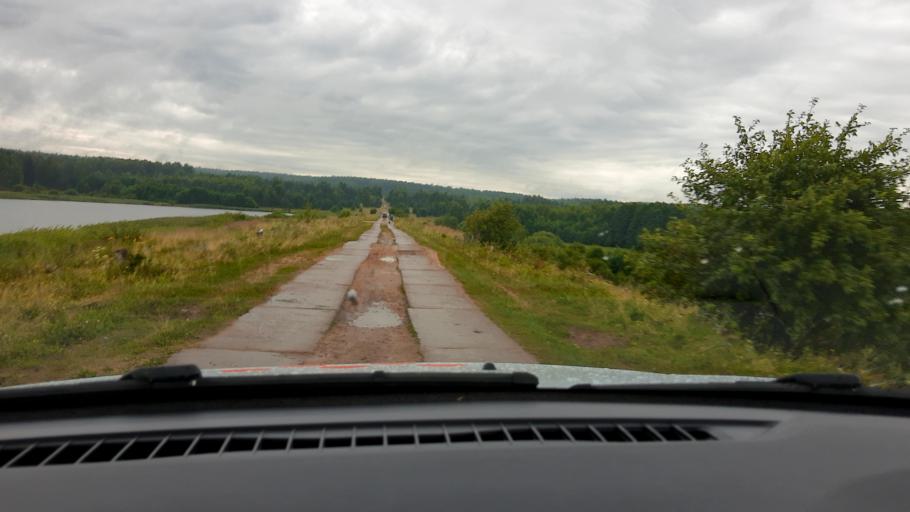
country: RU
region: Nizjnij Novgorod
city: Surovatikha
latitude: 55.9354
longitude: 43.9170
